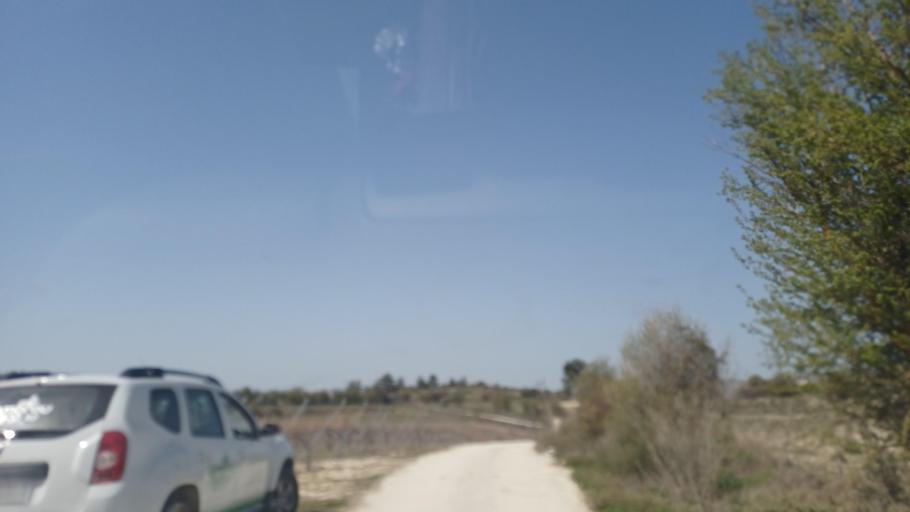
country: CY
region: Limassol
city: Pachna
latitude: 34.8783
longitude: 32.7026
